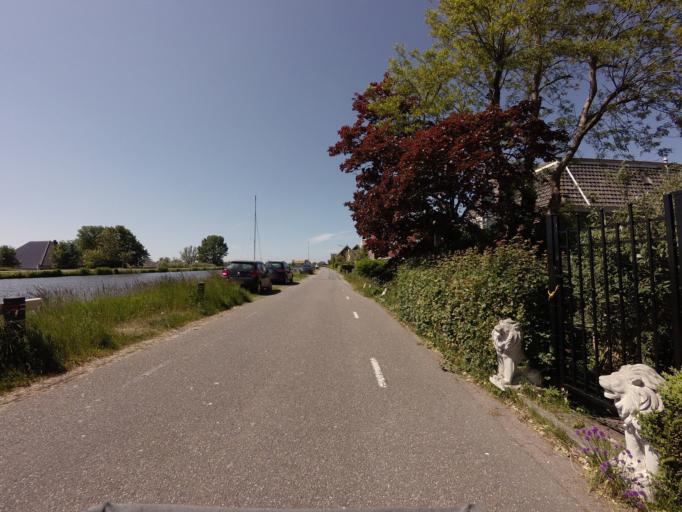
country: NL
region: North Holland
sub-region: Gemeente Zaanstad
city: Zaanstad
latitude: 52.5447
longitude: 4.8157
